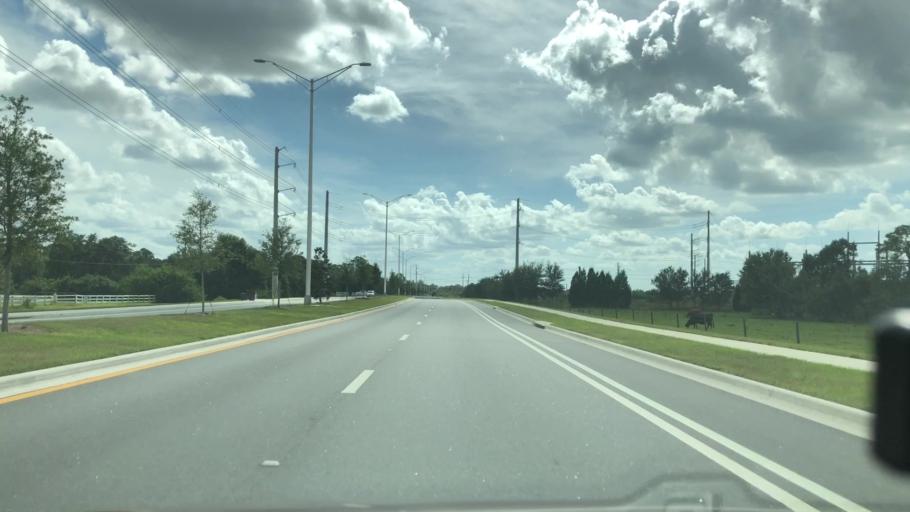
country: US
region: Florida
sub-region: Sarasota County
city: Lake Sarasota
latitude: 27.3452
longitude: -82.3837
